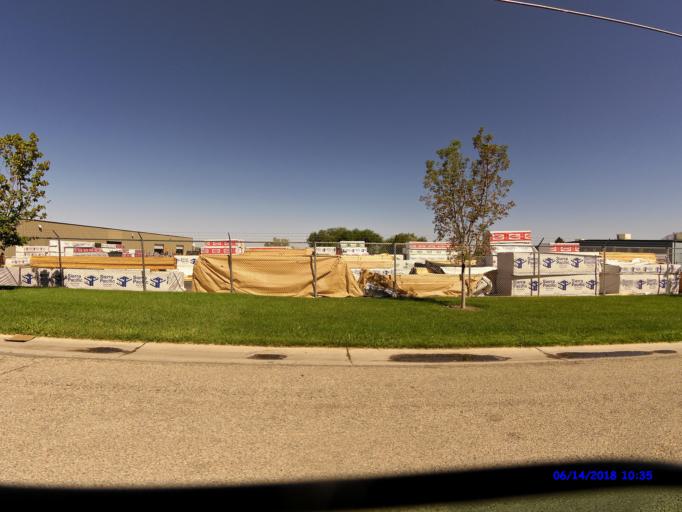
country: US
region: Utah
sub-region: Weber County
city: Riverdale
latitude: 41.2130
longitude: -112.0140
